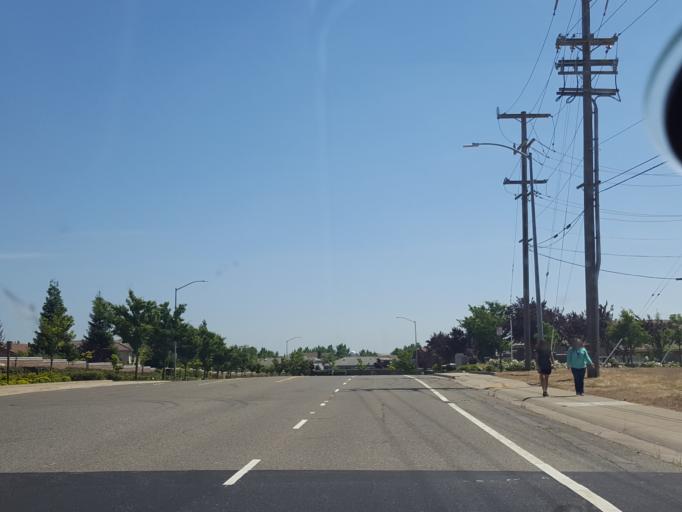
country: US
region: California
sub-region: Sacramento County
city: Rancho Cordova
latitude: 38.5831
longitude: -121.2704
